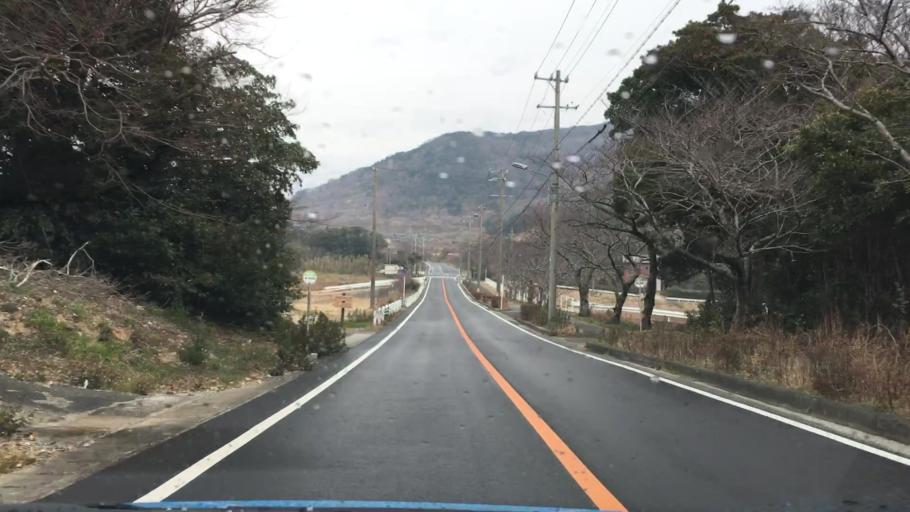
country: JP
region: Aichi
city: Tahara
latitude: 34.6773
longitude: 137.2492
